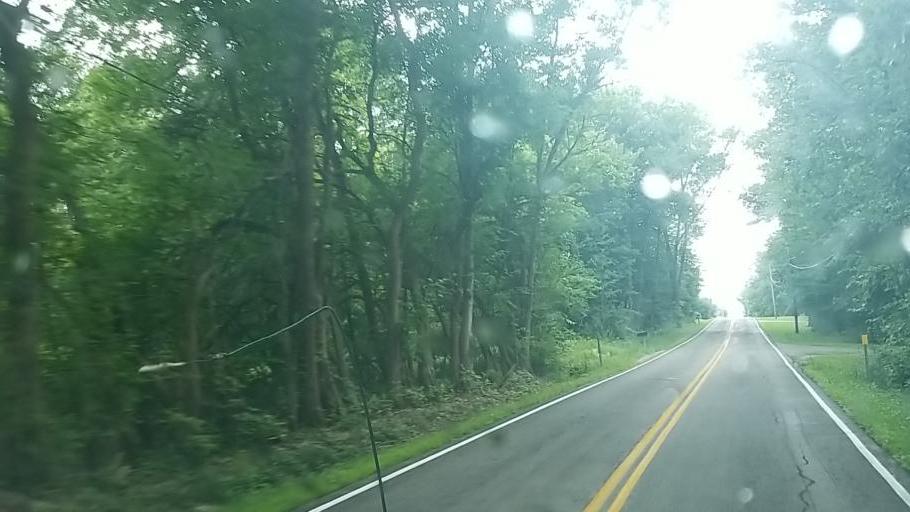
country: US
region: Ohio
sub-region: Lorain County
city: Lagrange
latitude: 41.1773
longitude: -82.0834
